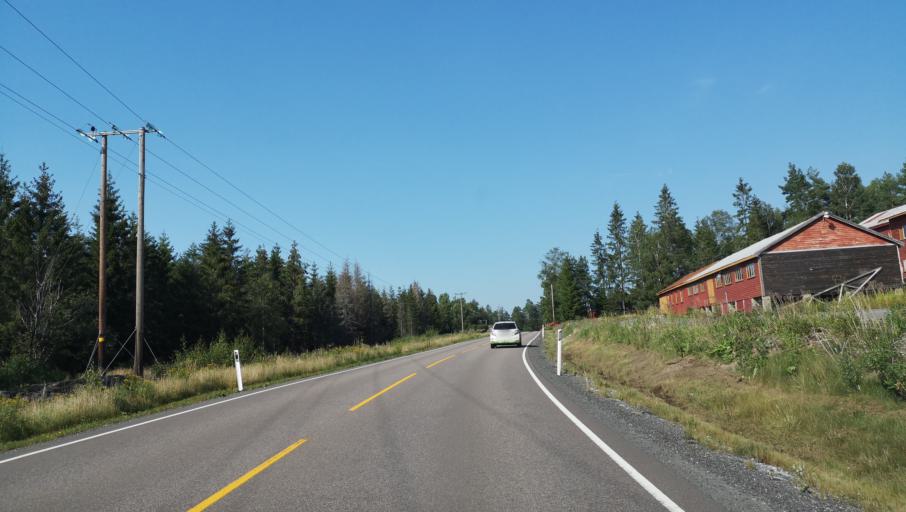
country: NO
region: Ostfold
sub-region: Valer
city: Kirkebygda
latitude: 59.5405
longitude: 10.8479
